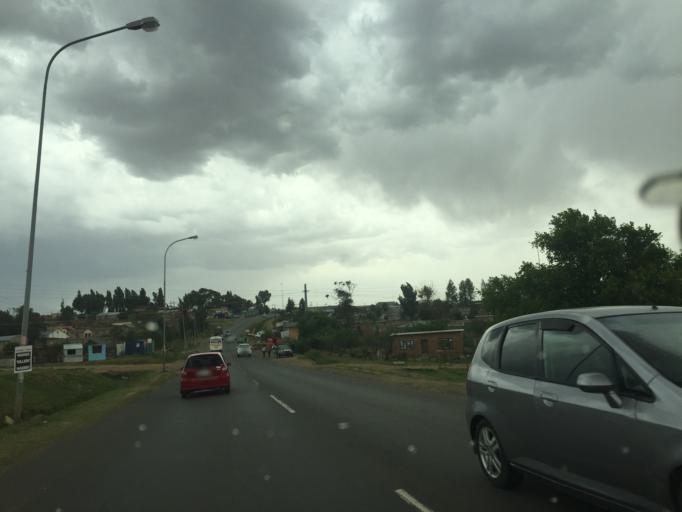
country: LS
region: Maseru
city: Maseru
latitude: -29.2797
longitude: 27.5287
